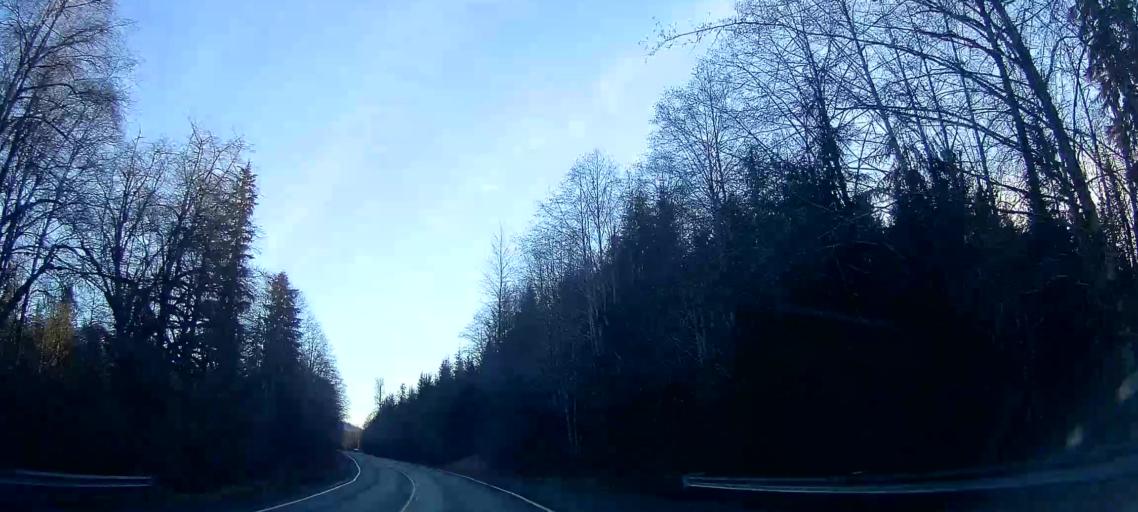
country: US
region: Washington
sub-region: Snohomish County
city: Darrington
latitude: 48.6331
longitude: -121.7405
